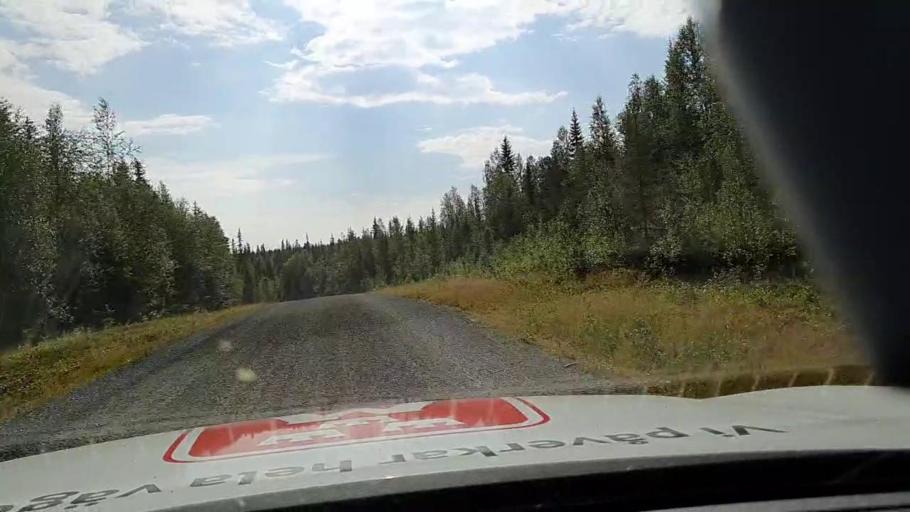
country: SE
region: Vaesterbotten
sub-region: Storumans Kommun
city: Fristad
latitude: 65.5414
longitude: 16.7983
